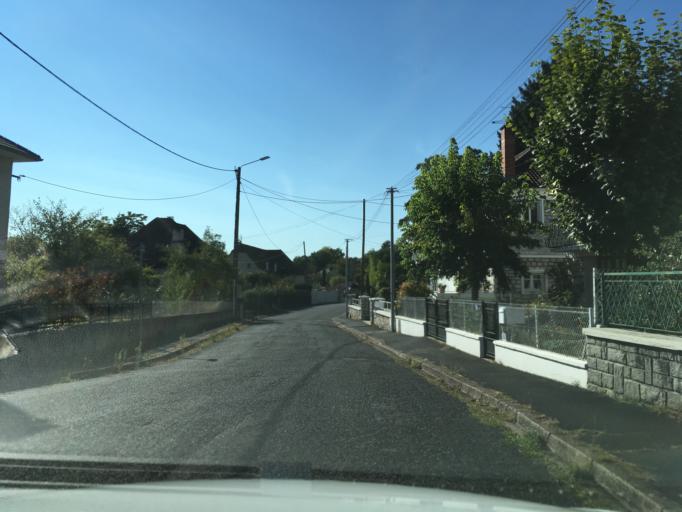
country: FR
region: Limousin
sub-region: Departement de la Correze
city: Malemort-sur-Correze
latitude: 45.1694
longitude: 1.5472
